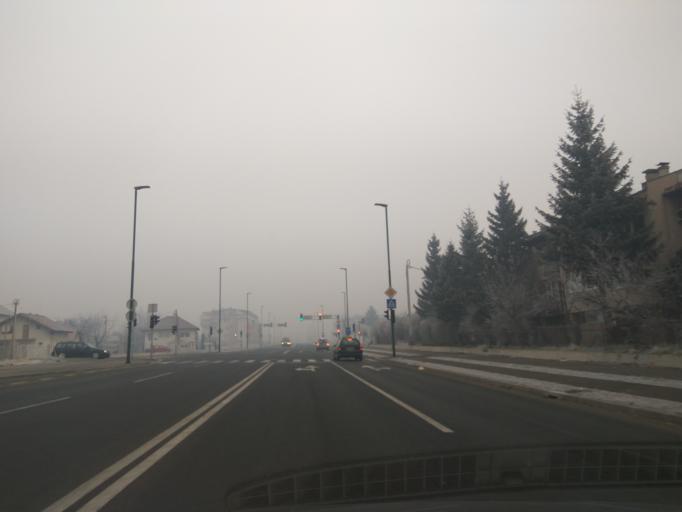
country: BA
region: Federation of Bosnia and Herzegovina
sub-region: Kanton Sarajevo
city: Sarajevo
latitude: 43.8307
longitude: 18.3358
